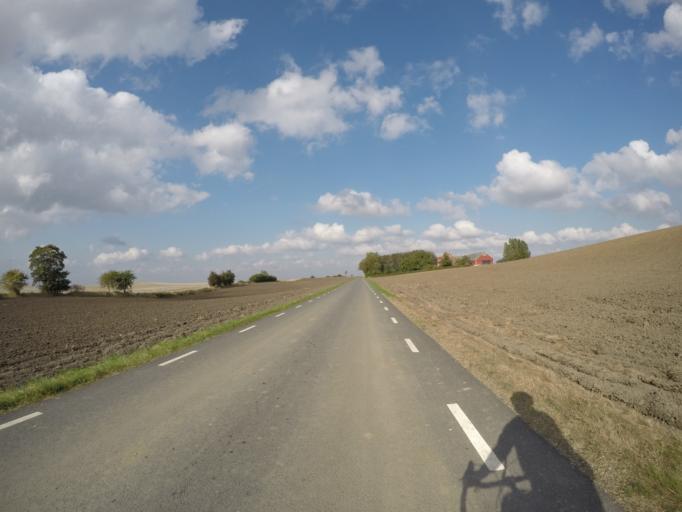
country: SE
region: Skane
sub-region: Svedala Kommun
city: Klagerup
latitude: 55.5924
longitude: 13.1999
